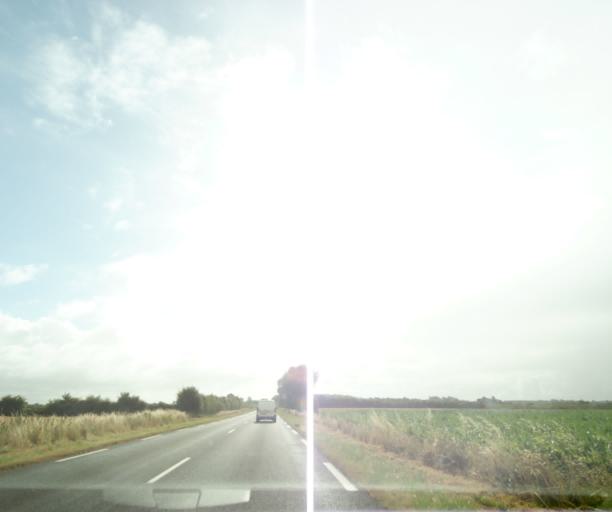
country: FR
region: Pays de la Loire
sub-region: Departement de la Vendee
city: Moutiers-les-Mauxfaits
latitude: 46.4544
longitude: -1.4006
